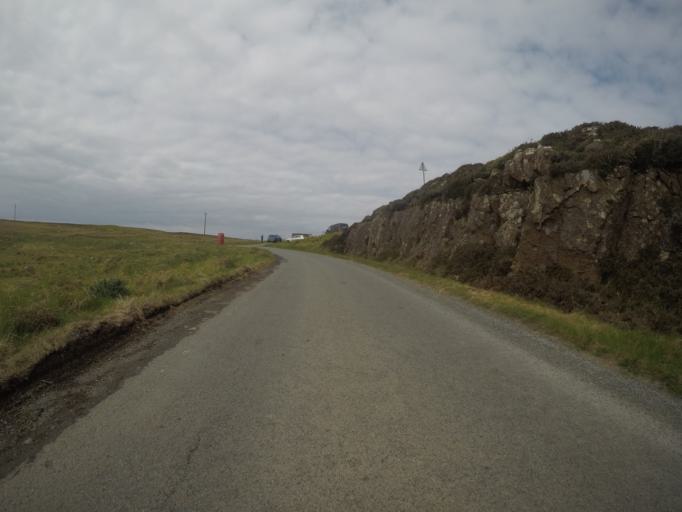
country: GB
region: Scotland
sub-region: Highland
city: Portree
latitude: 57.6839
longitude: -6.3262
